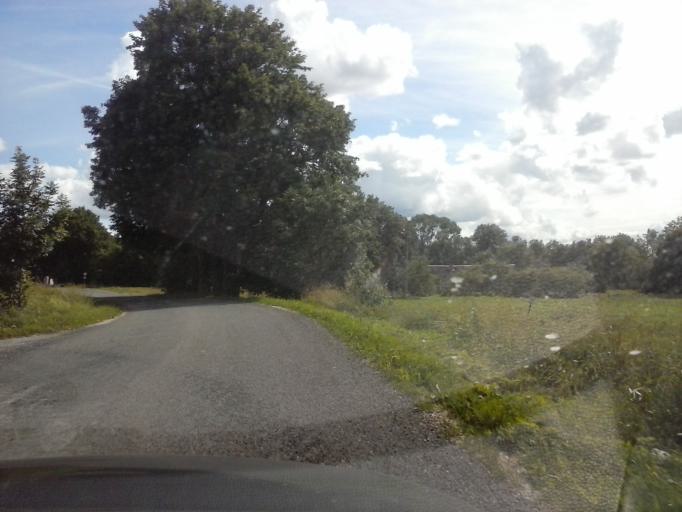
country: EE
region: Laeaene-Virumaa
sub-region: Vaeike-Maarja vald
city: Vaike-Maarja
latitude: 59.0807
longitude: 26.1947
